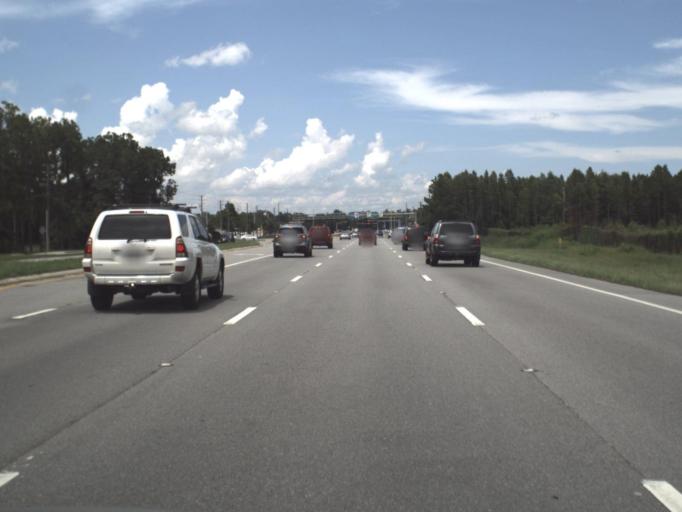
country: US
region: Florida
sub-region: Pasco County
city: Wesley Chapel
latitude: 28.2313
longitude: -82.3510
